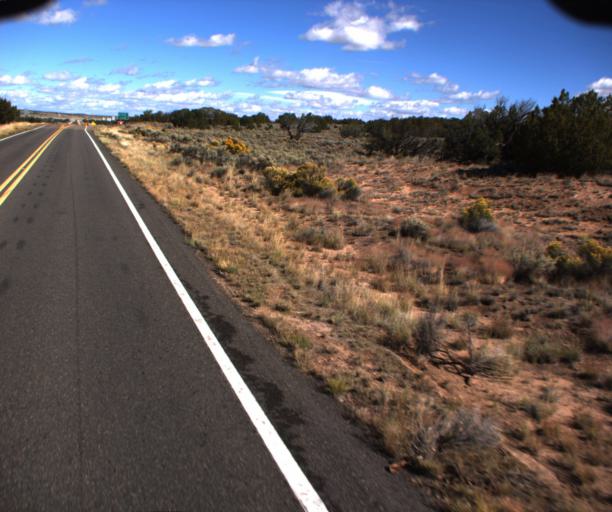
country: US
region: Arizona
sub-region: Apache County
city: Houck
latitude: 34.8994
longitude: -109.2381
